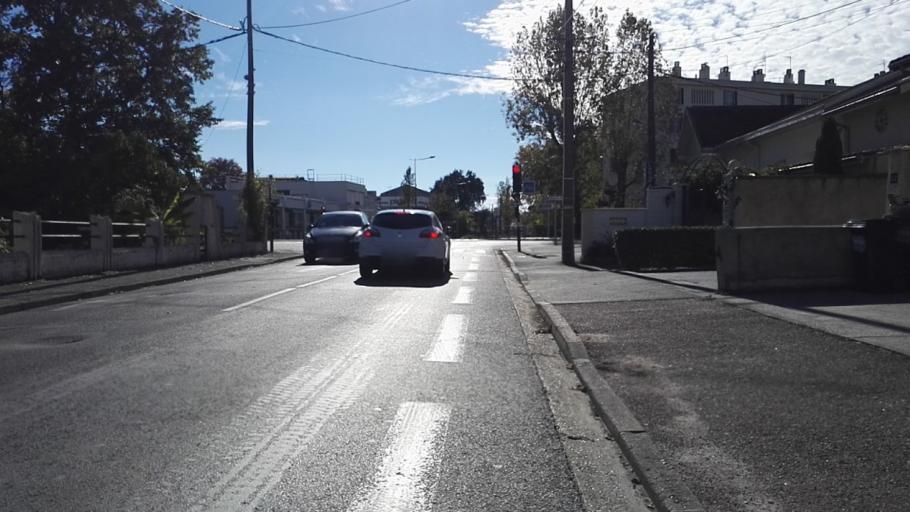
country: FR
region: Aquitaine
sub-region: Departement de la Gironde
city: Merignac
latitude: 44.8447
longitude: -0.6449
